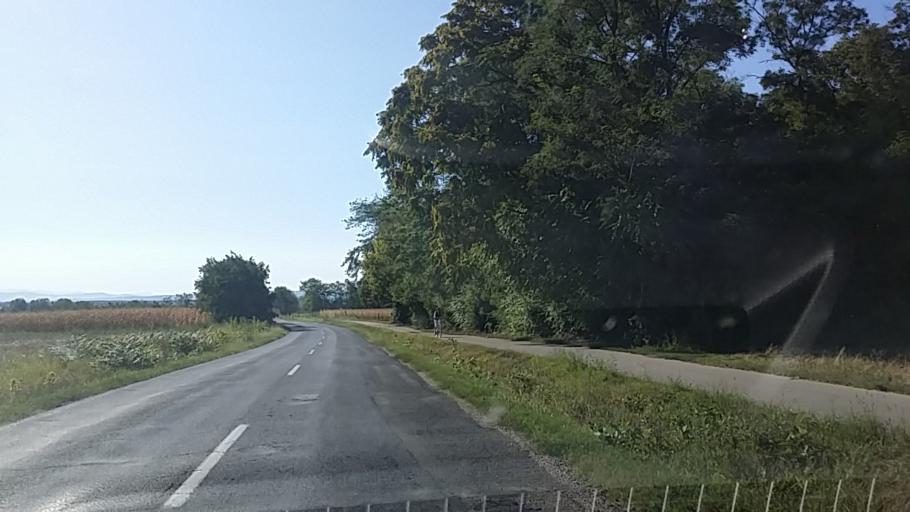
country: HU
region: Gyor-Moson-Sopron
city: Fertod
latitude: 47.6168
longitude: 16.8181
